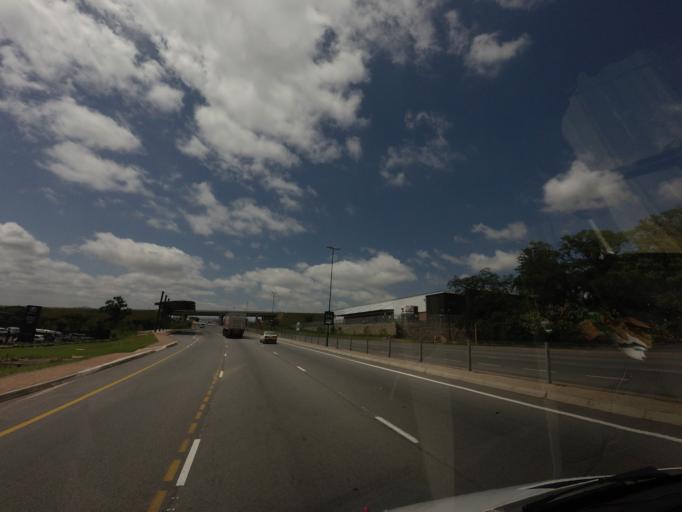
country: ZA
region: Mpumalanga
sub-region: Ehlanzeni District
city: Nelspruit
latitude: -25.4318
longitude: 30.9645
